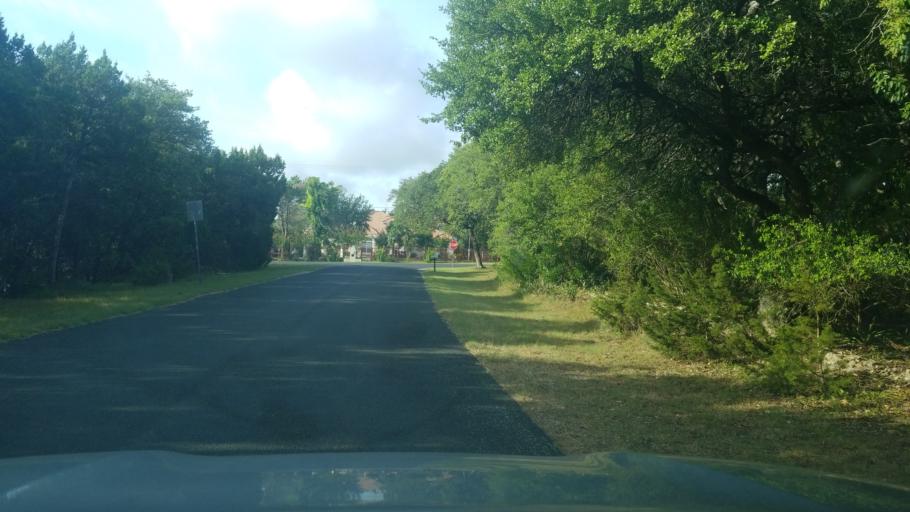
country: US
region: Texas
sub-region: Bexar County
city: Timberwood Park
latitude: 29.6977
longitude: -98.5180
